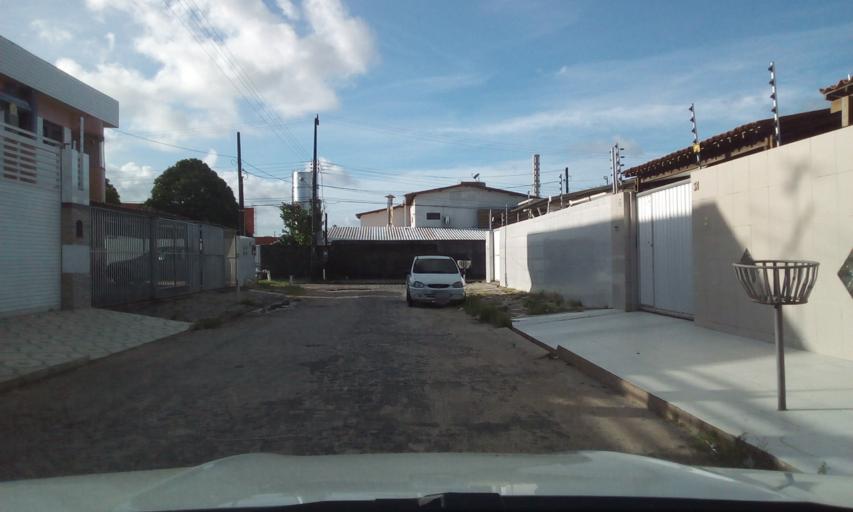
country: BR
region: Paraiba
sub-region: Joao Pessoa
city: Joao Pessoa
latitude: -7.1726
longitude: -34.8641
